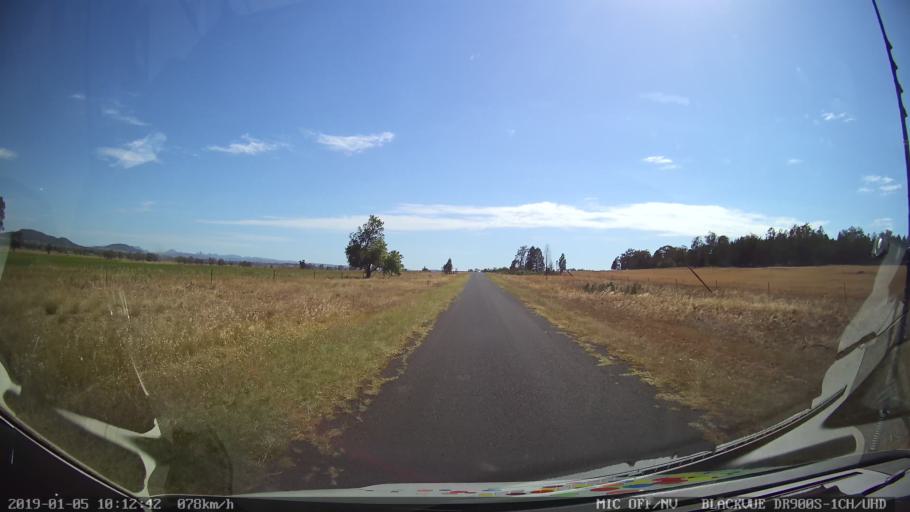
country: AU
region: New South Wales
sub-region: Gilgandra
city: Gilgandra
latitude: -31.6060
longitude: 148.9160
